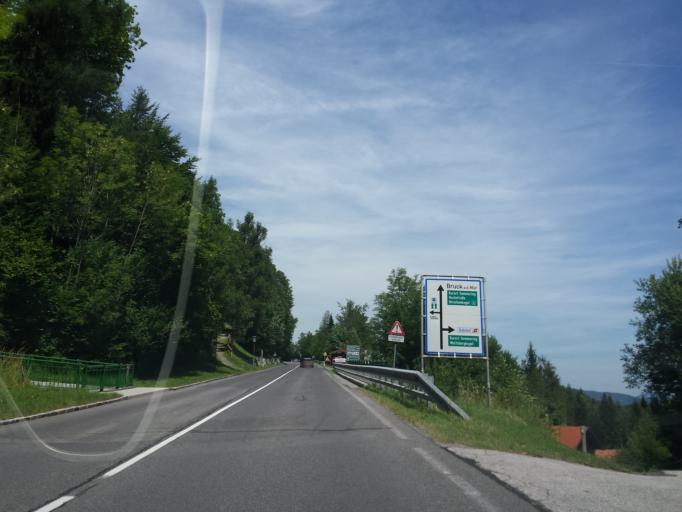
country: AT
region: Lower Austria
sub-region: Politischer Bezirk Neunkirchen
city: Semmering
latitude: 47.6334
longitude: 15.8332
